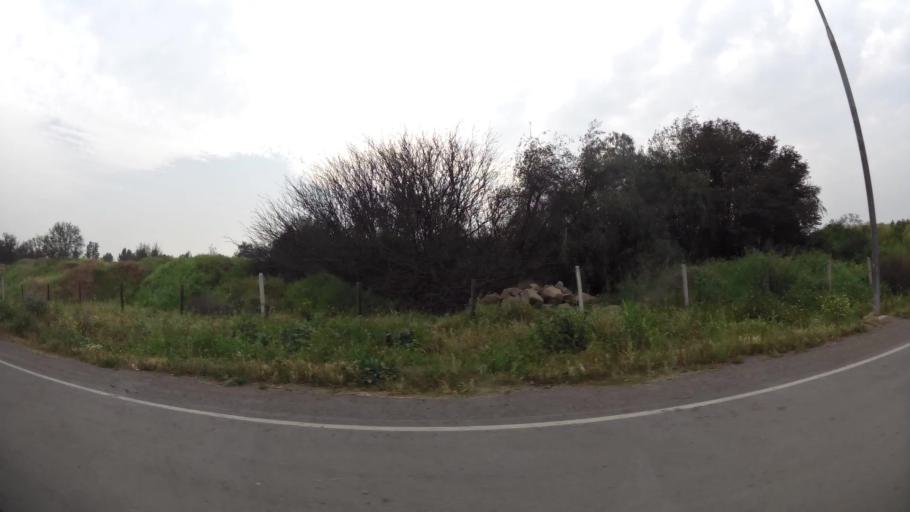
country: CL
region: Santiago Metropolitan
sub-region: Provincia de Chacabuco
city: Chicureo Abajo
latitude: -33.2204
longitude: -70.6781
